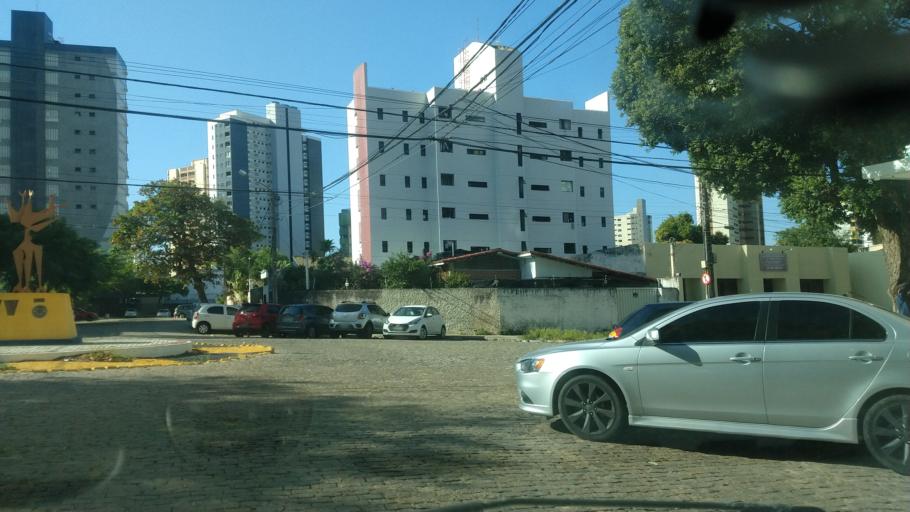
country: BR
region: Rio Grande do Norte
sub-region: Natal
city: Natal
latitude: -5.7828
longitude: -35.1978
